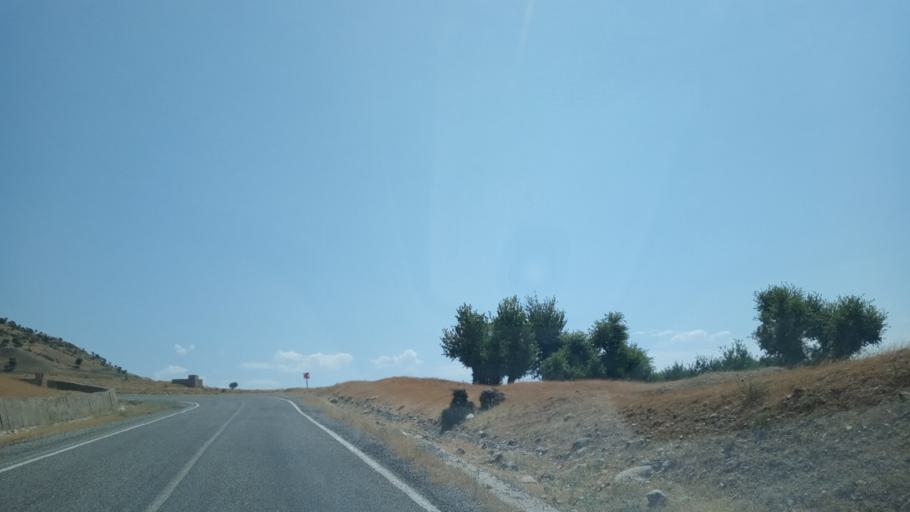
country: TR
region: Siirt
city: Dilektepe
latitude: 38.0630
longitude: 41.8320
